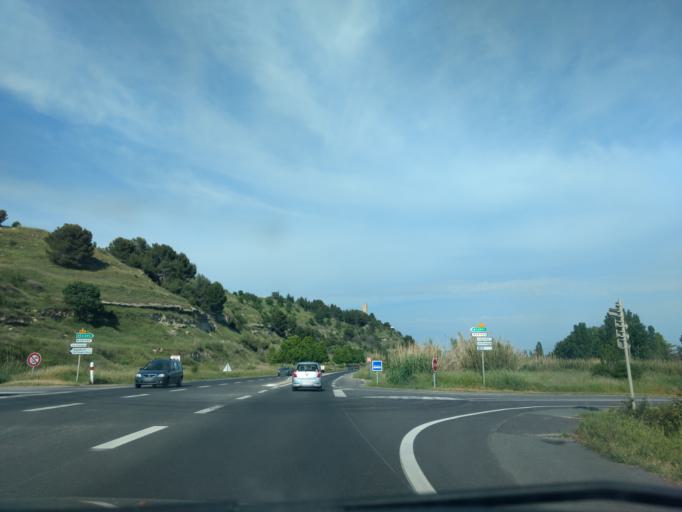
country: FR
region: Languedoc-Roussillon
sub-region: Departement de l'Herault
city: Montady
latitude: 43.3288
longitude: 3.1109
